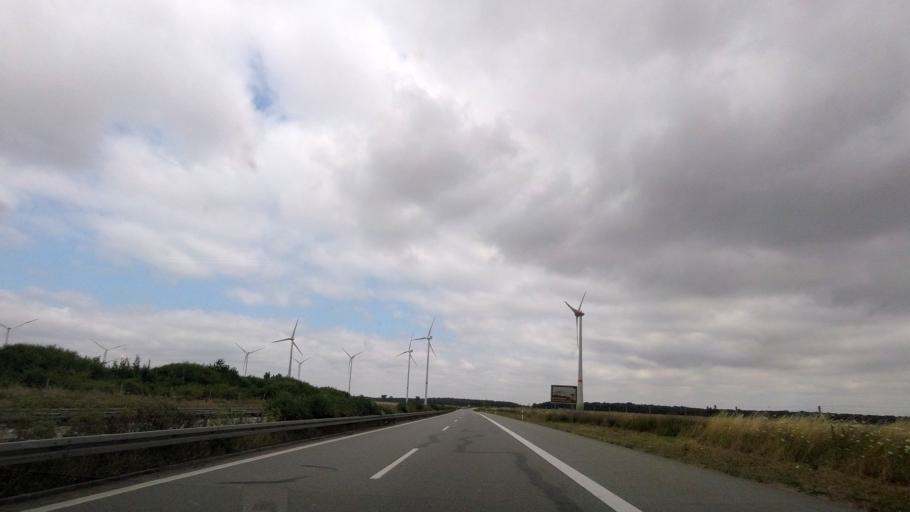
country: DE
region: Mecklenburg-Vorpommern
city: Jarmen
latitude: 53.8822
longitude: 13.3458
